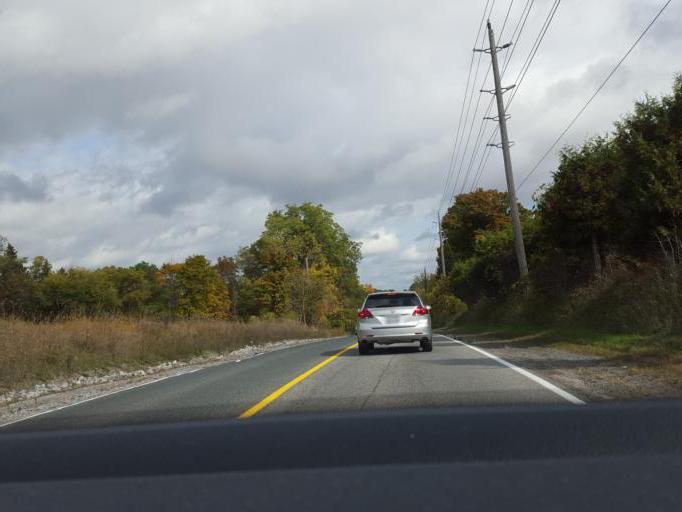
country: CA
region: Ontario
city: Markham
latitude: 43.8475
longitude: -79.2035
